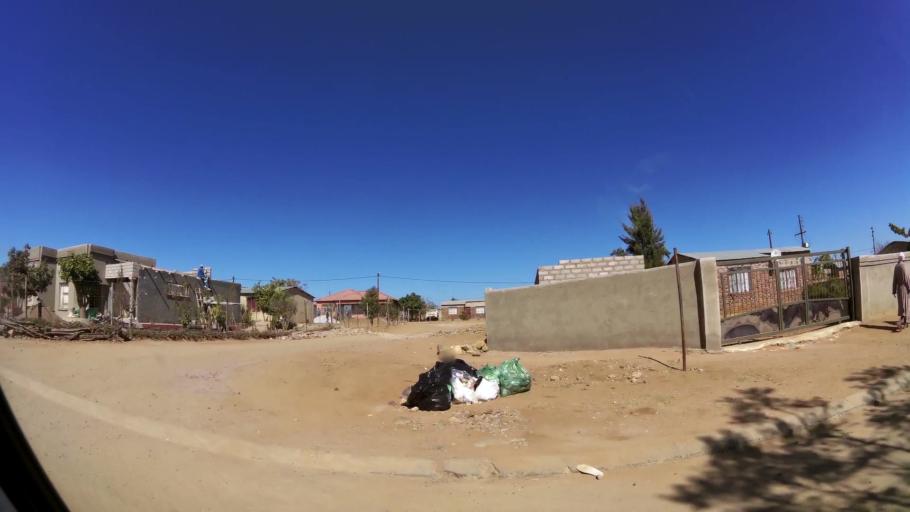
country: ZA
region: Limpopo
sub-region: Capricorn District Municipality
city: Polokwane
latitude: -23.8763
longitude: 29.4120
